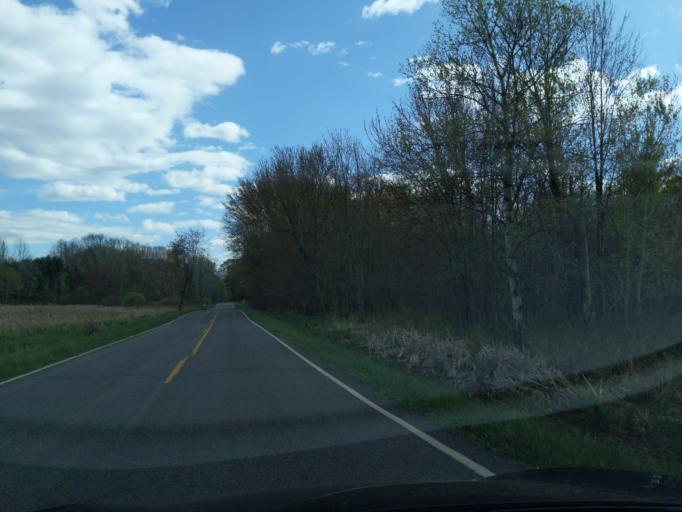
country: US
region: Michigan
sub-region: Ingham County
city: Leslie
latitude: 42.4012
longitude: -84.5417
